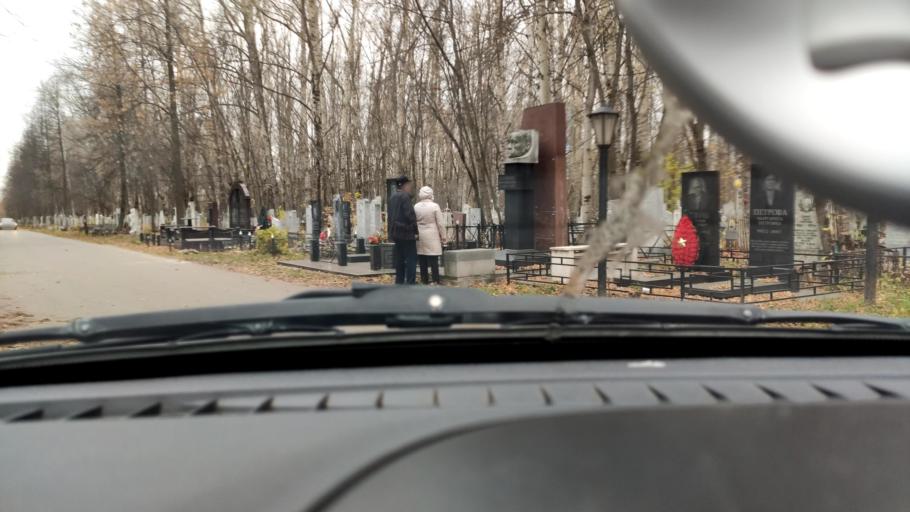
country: RU
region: Perm
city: Perm
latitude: 57.9902
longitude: 56.2848
